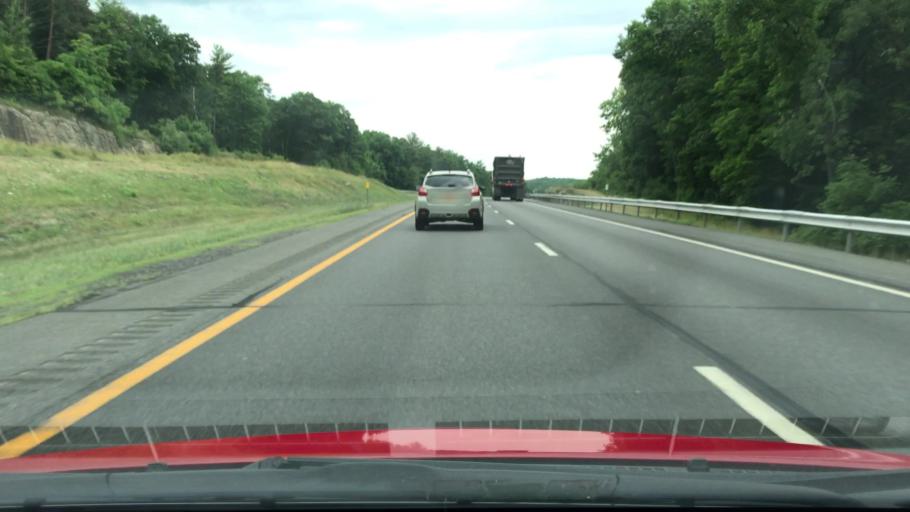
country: US
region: New York
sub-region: Greene County
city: Jefferson Heights
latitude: 42.3009
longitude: -73.8743
